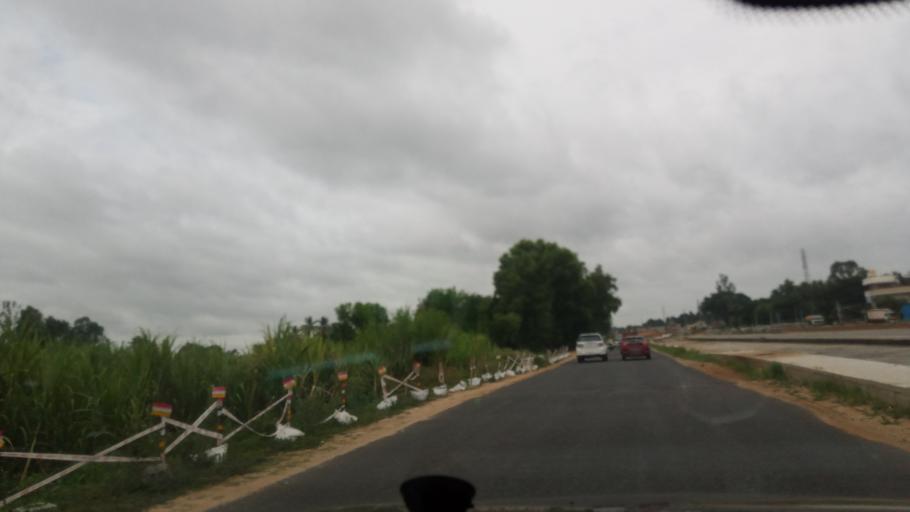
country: IN
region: Karnataka
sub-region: Mandya
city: Mandya
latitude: 12.5090
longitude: 76.8406
